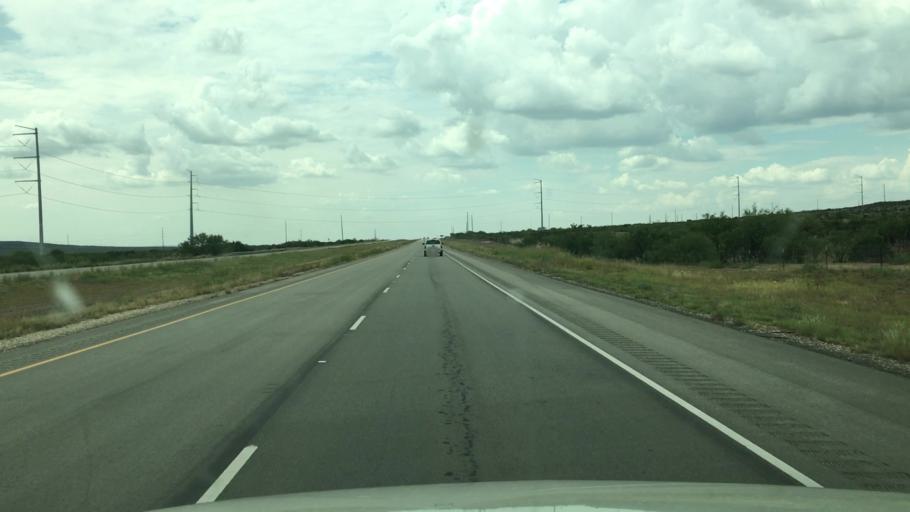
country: US
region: Texas
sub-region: Glasscock County
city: Garden City
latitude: 31.9849
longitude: -101.2605
